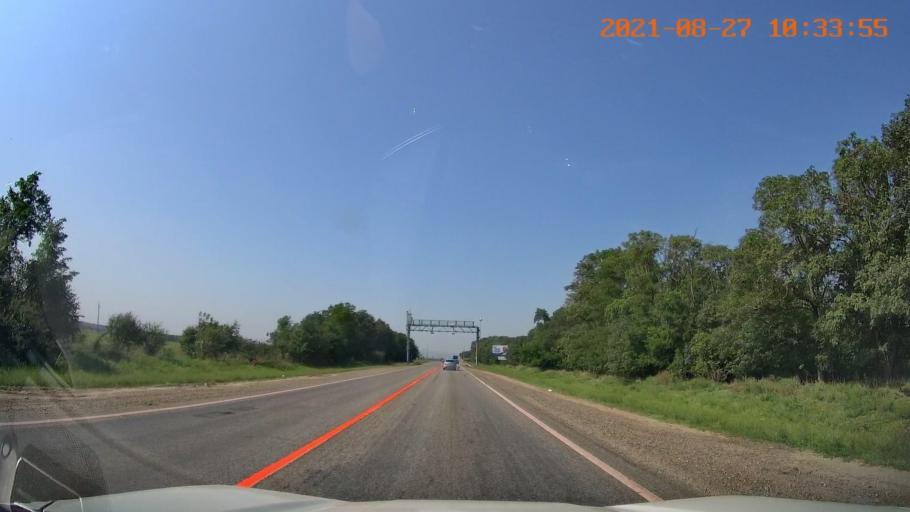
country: RU
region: Karachayevo-Cherkesiya
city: Cherkessk
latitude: 44.2572
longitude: 42.1143
